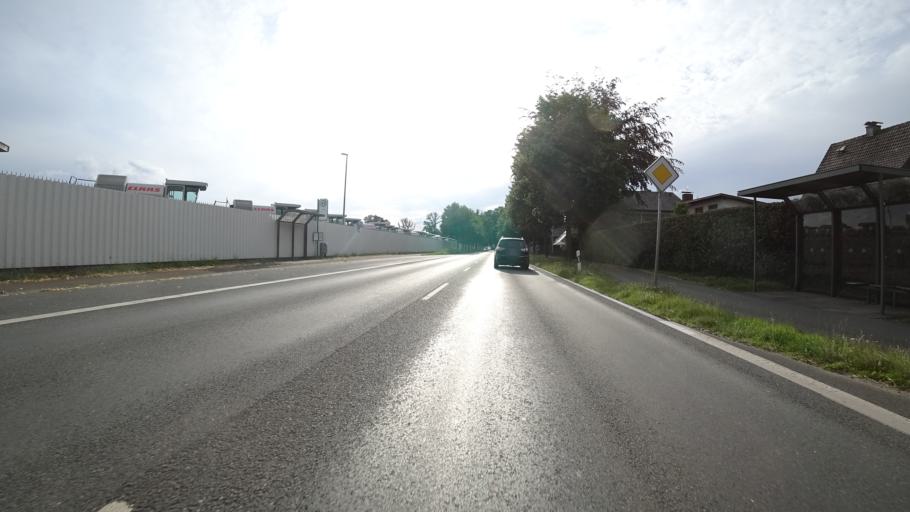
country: DE
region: North Rhine-Westphalia
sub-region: Regierungsbezirk Detmold
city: Harsewinkel
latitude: 51.9640
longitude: 8.2044
